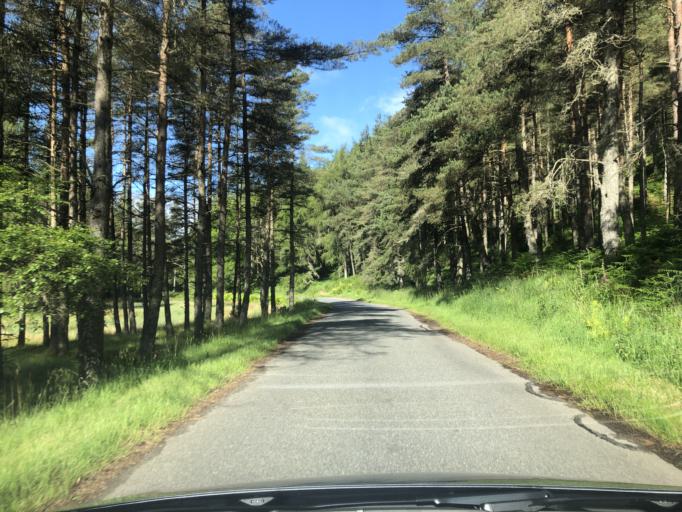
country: GB
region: Scotland
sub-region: Angus
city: Kirriemuir
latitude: 56.7339
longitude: -3.0211
